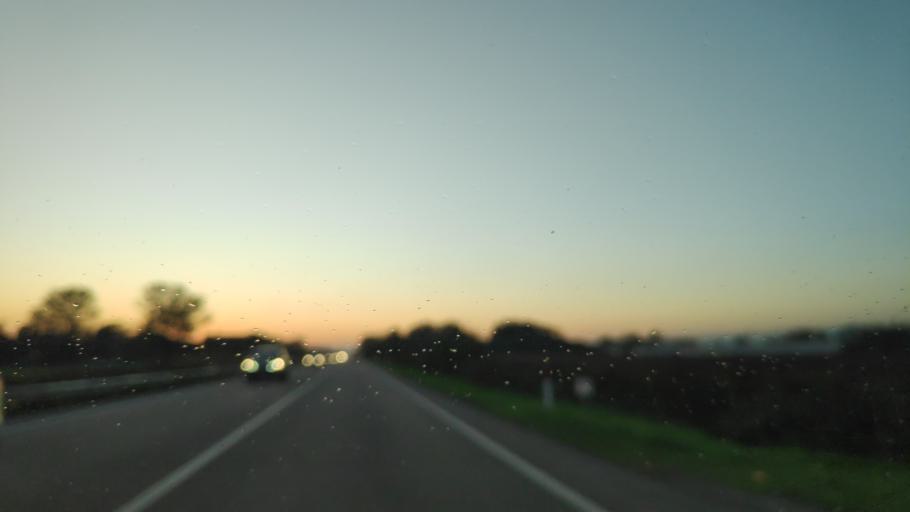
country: IT
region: Lombardy
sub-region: Citta metropolitana di Milano
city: Gaggiano
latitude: 45.4056
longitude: 9.0195
